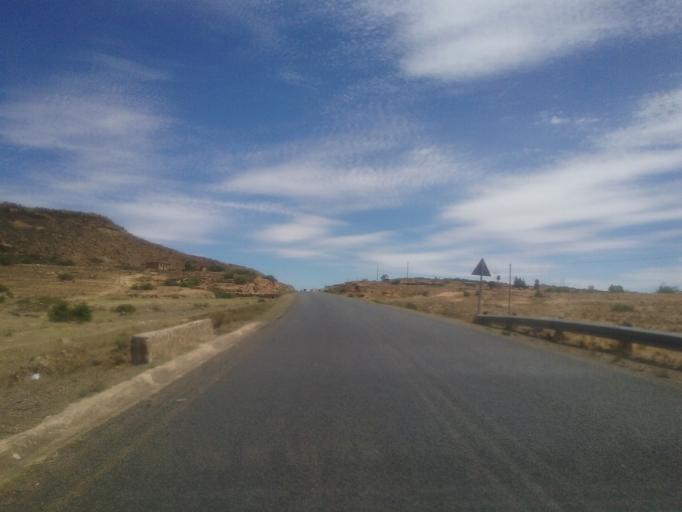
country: LS
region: Mohale's Hoek District
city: Mohale's Hoek
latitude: -30.0715
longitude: 27.4240
